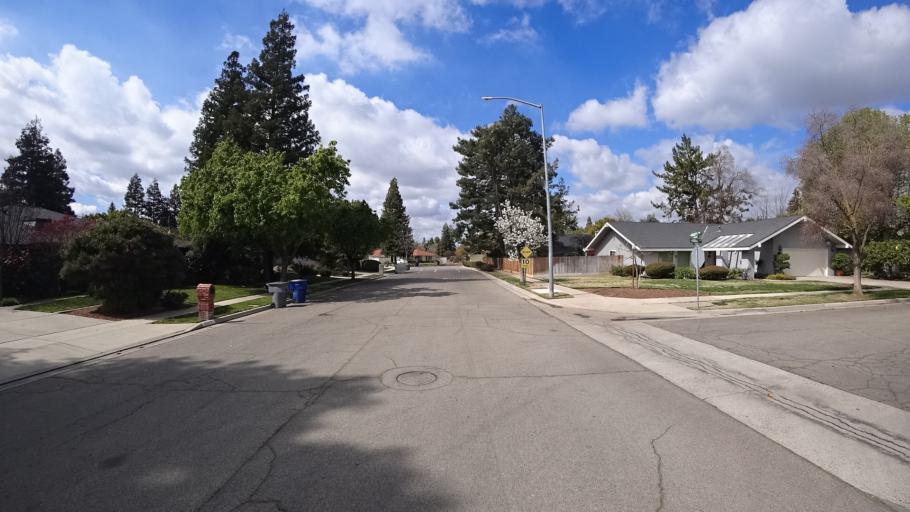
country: US
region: California
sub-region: Fresno County
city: Fresno
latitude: 36.8336
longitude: -119.8585
